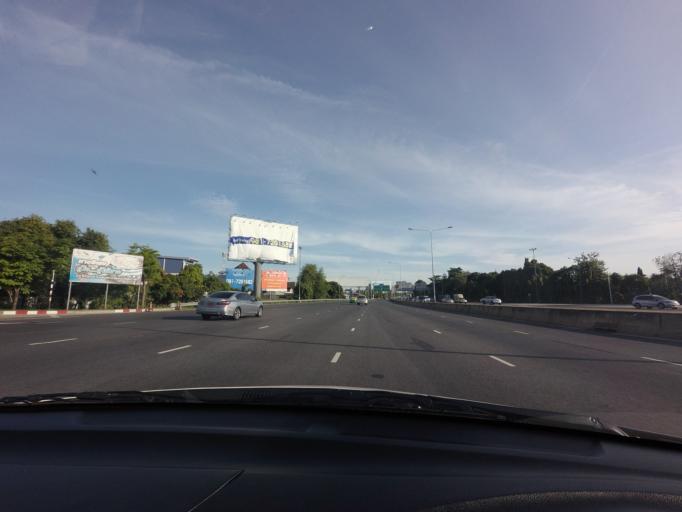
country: TH
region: Bangkok
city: Chatuchak
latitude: 13.8389
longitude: 100.5355
